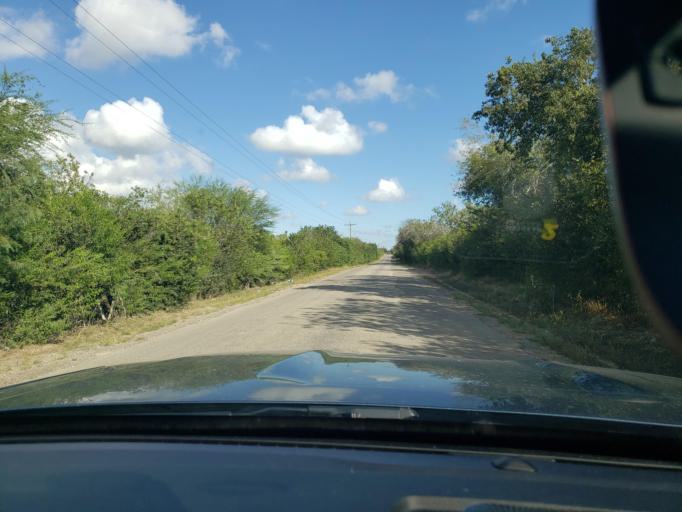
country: US
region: Texas
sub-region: Bee County
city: Beeville
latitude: 28.4534
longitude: -97.7177
